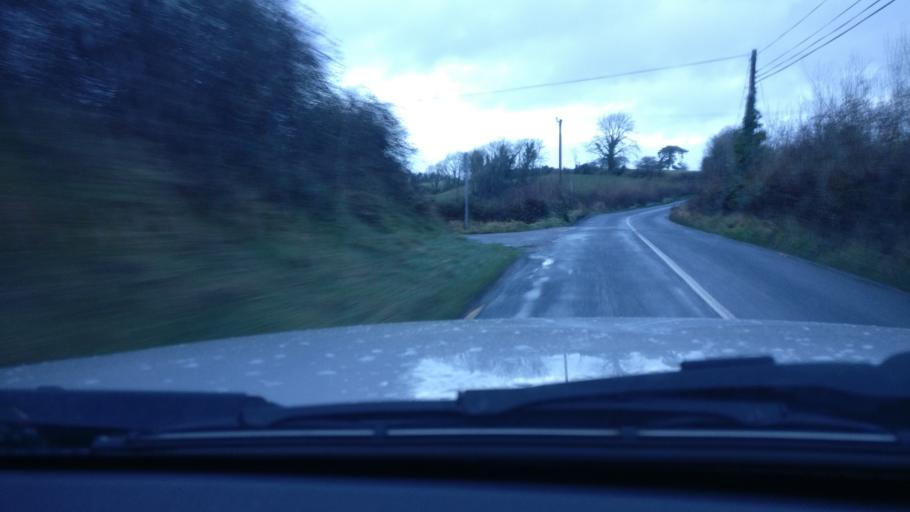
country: IE
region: Connaught
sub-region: County Galway
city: Ballinasloe
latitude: 53.2537
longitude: -8.2624
